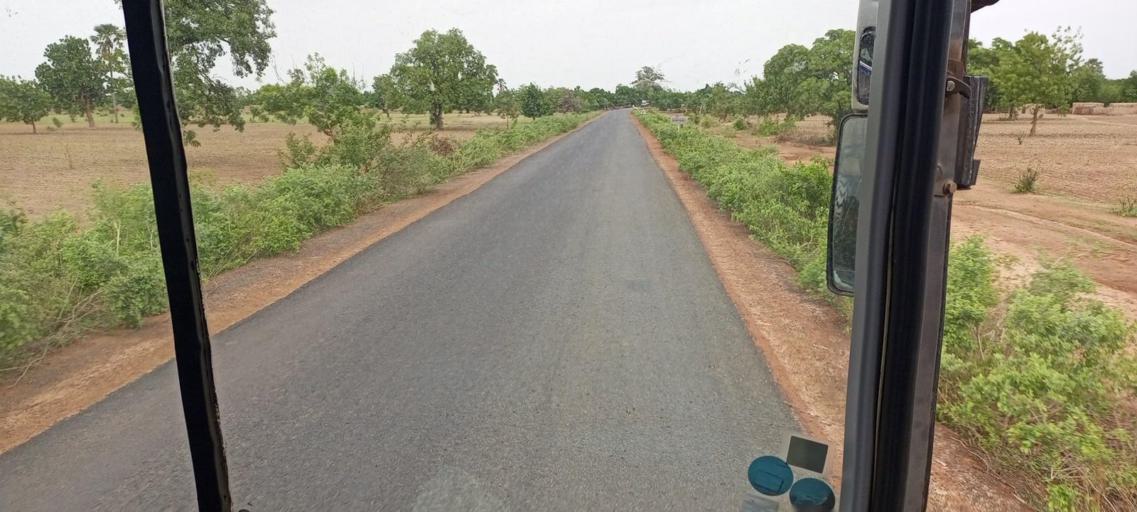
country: ML
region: Segou
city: Bla
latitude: 12.7400
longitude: -5.7282
